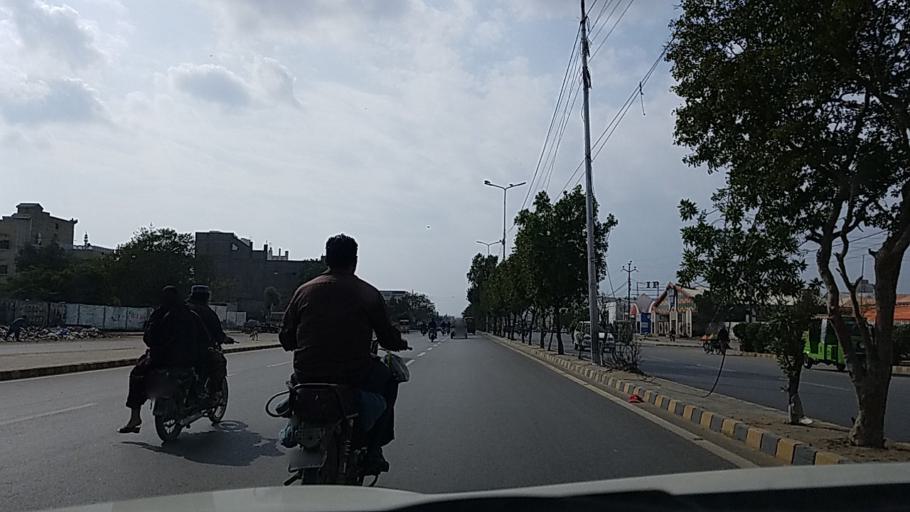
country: PK
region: Sindh
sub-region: Karachi District
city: Karachi
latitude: 24.8199
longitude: 67.1224
